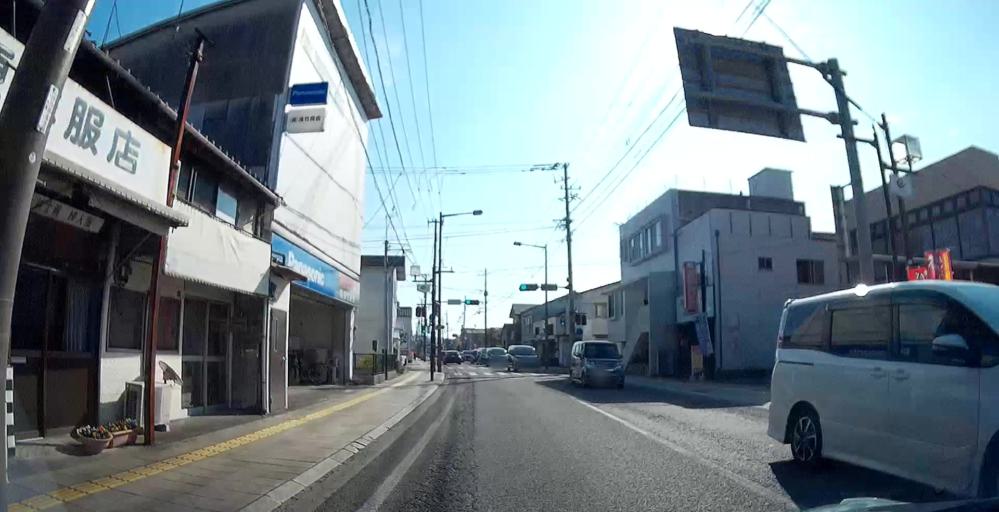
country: JP
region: Kumamoto
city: Uto
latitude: 32.7438
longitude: 130.6818
